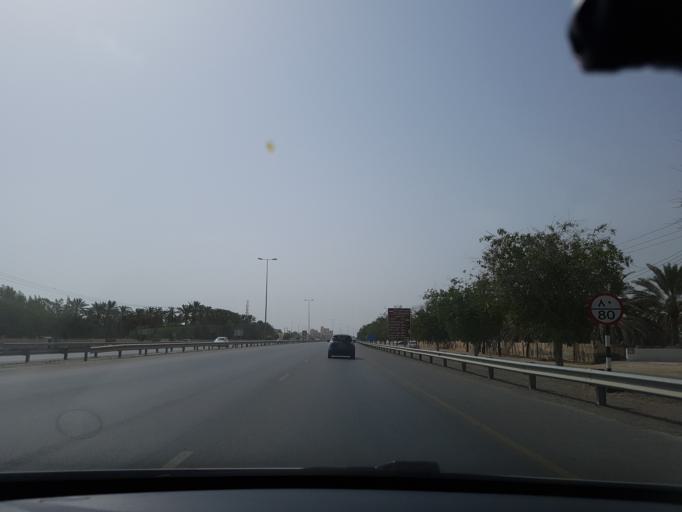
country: OM
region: Al Batinah
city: Al Khaburah
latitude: 23.9793
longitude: 57.0839
